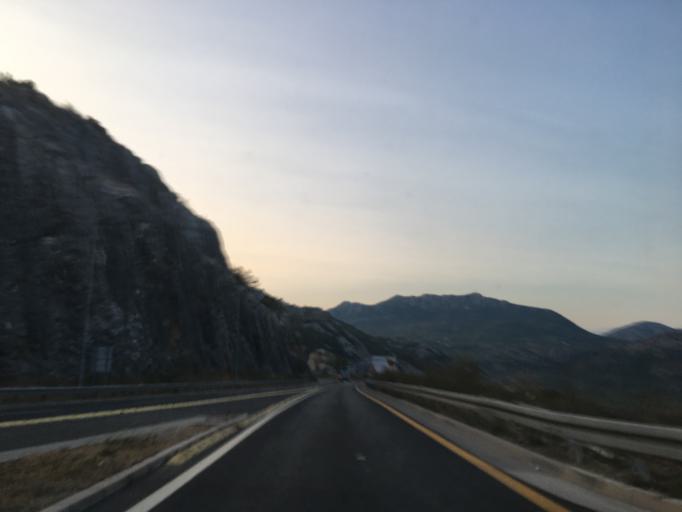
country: ME
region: Bar
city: Sutomore
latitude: 42.2045
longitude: 19.0505
